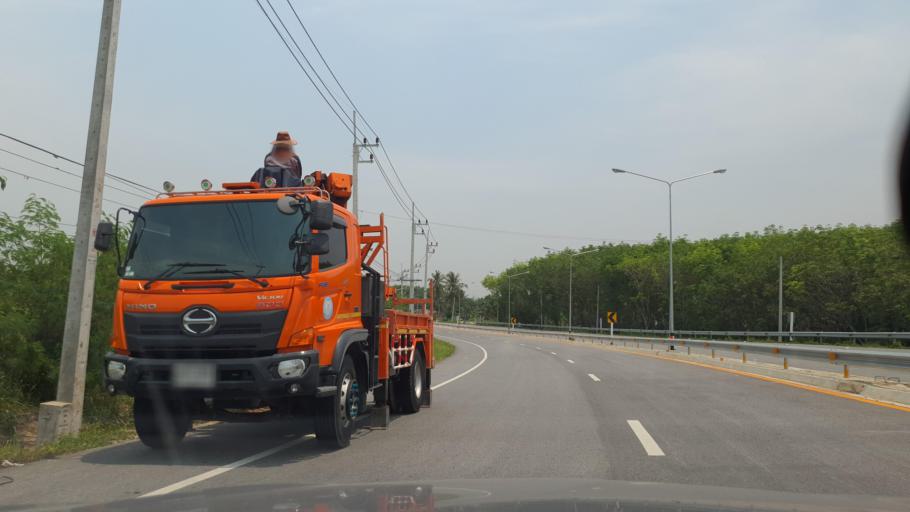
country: TH
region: Rayong
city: Ban Chang
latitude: 12.7759
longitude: 101.0258
